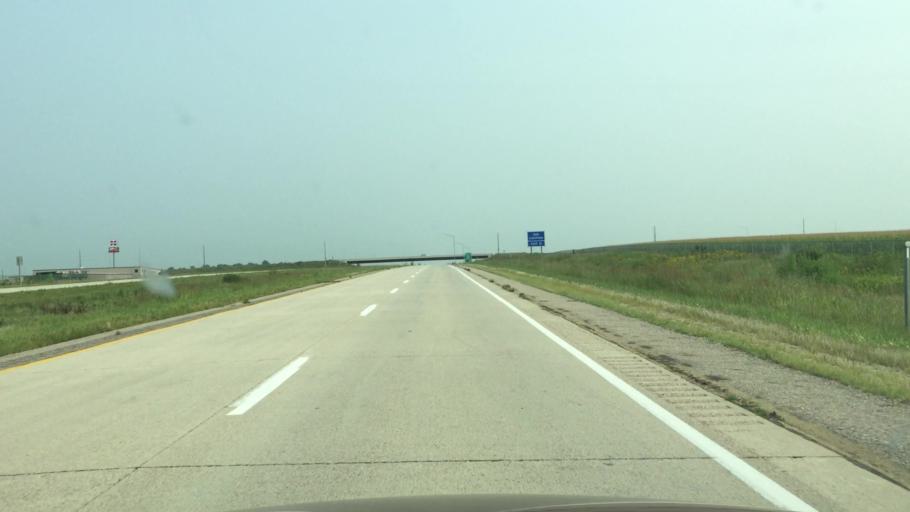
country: US
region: Iowa
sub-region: Osceola County
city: Sibley
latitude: 43.3992
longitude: -95.7171
